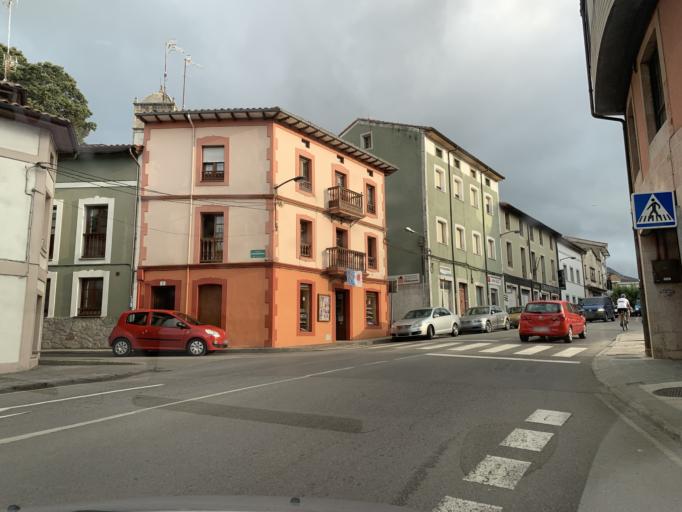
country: ES
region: Asturias
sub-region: Province of Asturias
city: Llanes
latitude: 43.4260
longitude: -4.8611
